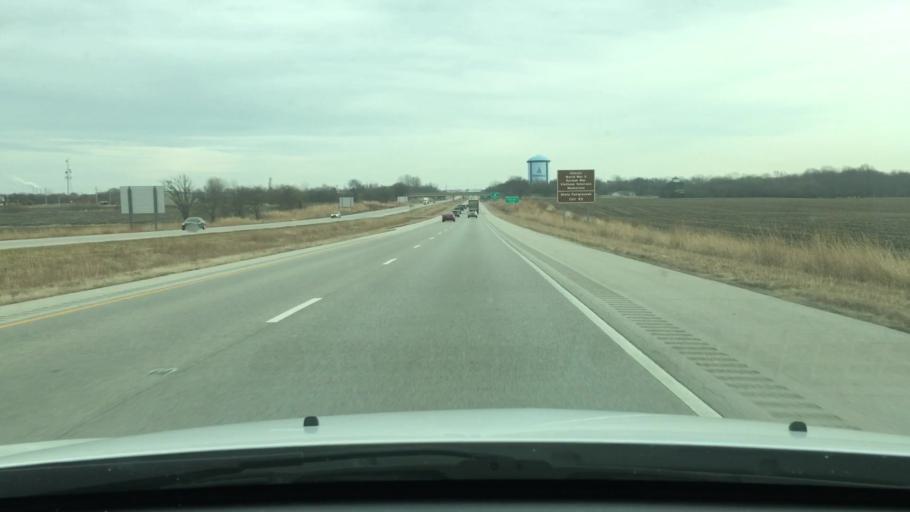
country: US
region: Illinois
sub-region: Sangamon County
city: Jerome
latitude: 39.7493
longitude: -89.7276
